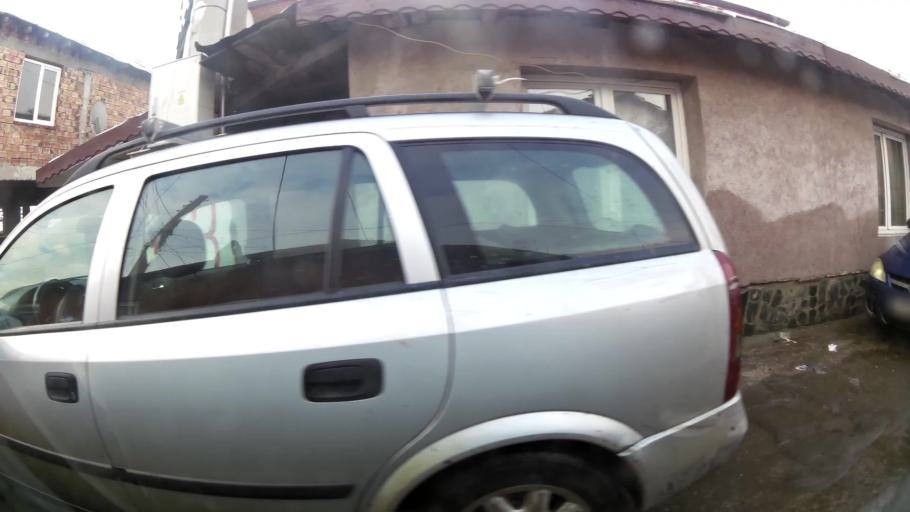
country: BG
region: Sofia-Capital
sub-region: Stolichna Obshtina
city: Sofia
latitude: 42.6934
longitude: 23.2641
